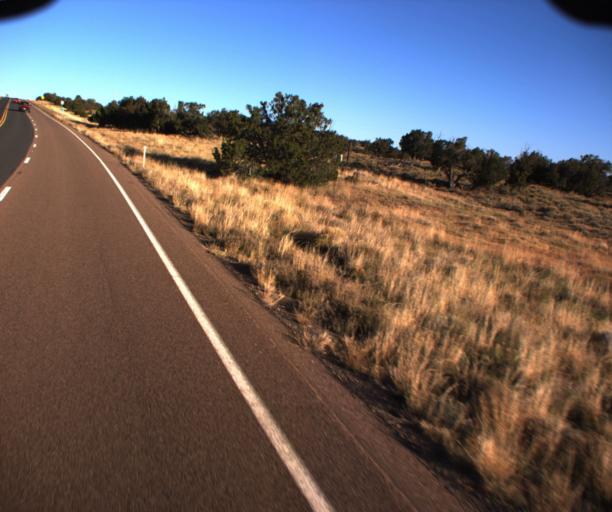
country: US
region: Arizona
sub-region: Apache County
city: Ganado
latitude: 35.4285
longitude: -109.5169
